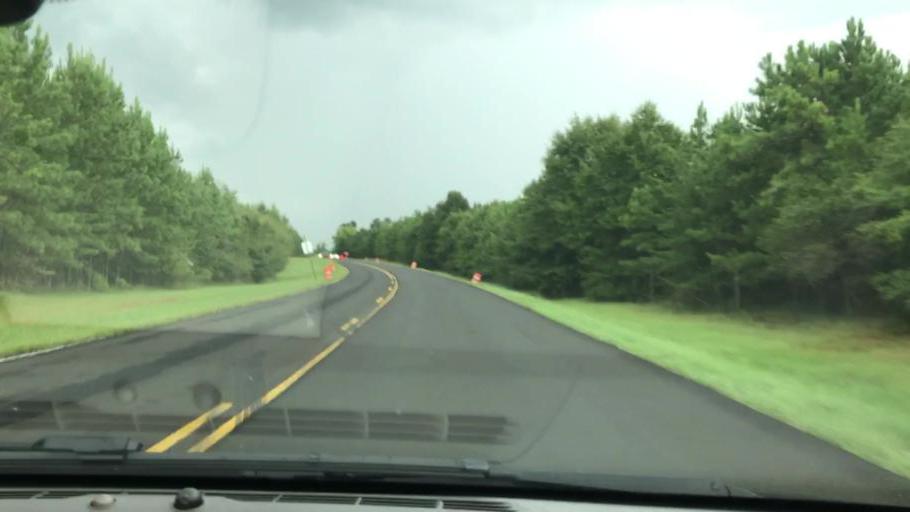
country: US
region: Georgia
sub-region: Clay County
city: Fort Gaines
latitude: 31.5104
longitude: -85.0209
